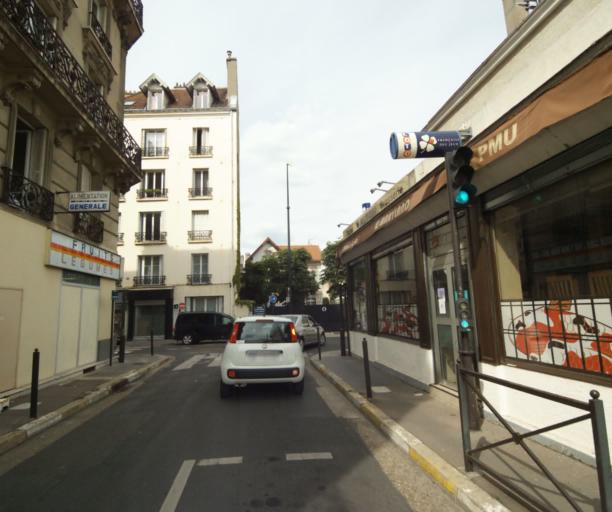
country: FR
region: Ile-de-France
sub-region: Departement des Hauts-de-Seine
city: Bois-Colombes
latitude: 48.9193
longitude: 2.2672
